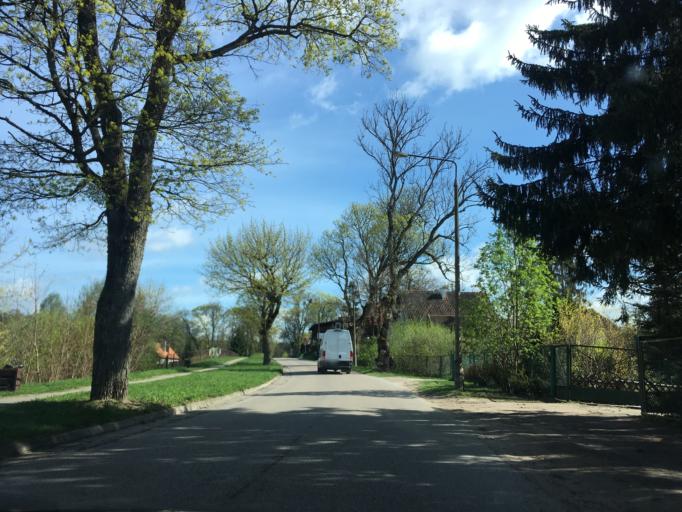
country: PL
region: Warmian-Masurian Voivodeship
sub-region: Powiat piski
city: Ruciane-Nida
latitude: 53.6599
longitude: 21.5661
